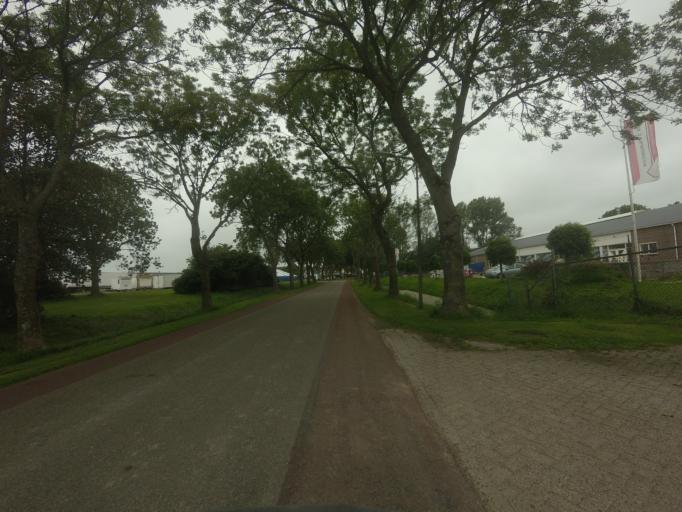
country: NL
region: Friesland
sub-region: Gemeente Ferwerderadiel
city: Ferwert
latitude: 53.3362
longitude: 5.8310
